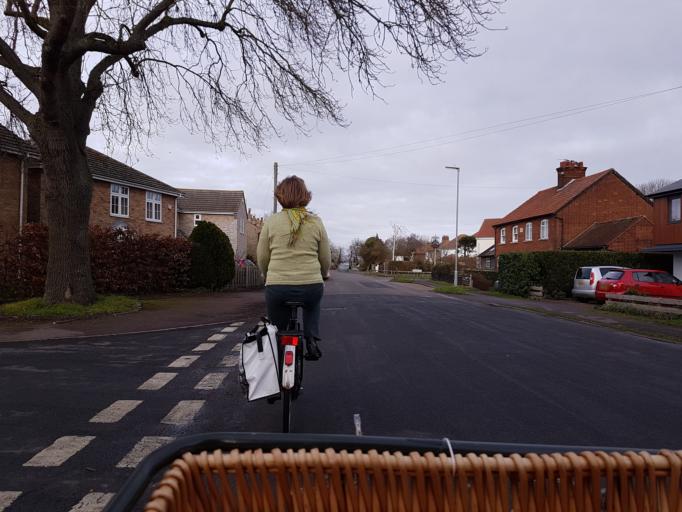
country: GB
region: England
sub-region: Cambridgeshire
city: Girton
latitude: 52.2377
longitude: 0.0847
